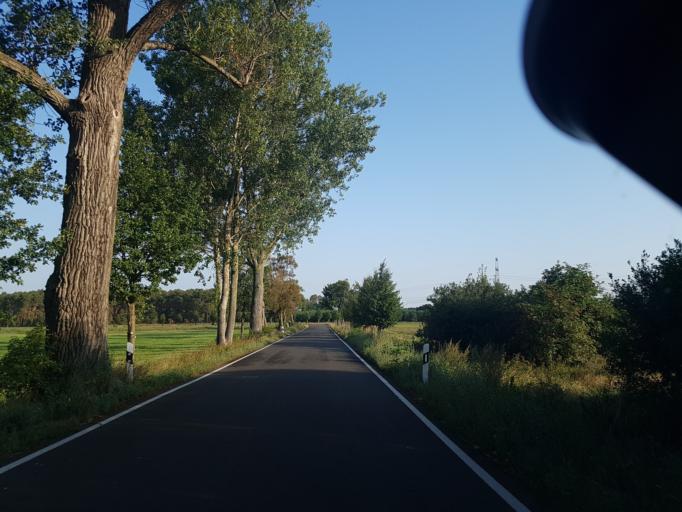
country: DE
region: Saxony-Anhalt
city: Holzdorf
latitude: 51.8251
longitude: 13.1410
